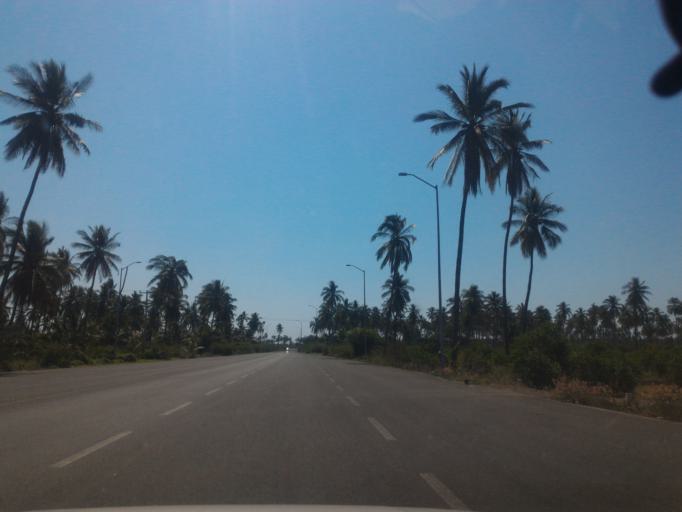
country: MX
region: Colima
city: Tecoman
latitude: 18.9026
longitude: -103.9058
